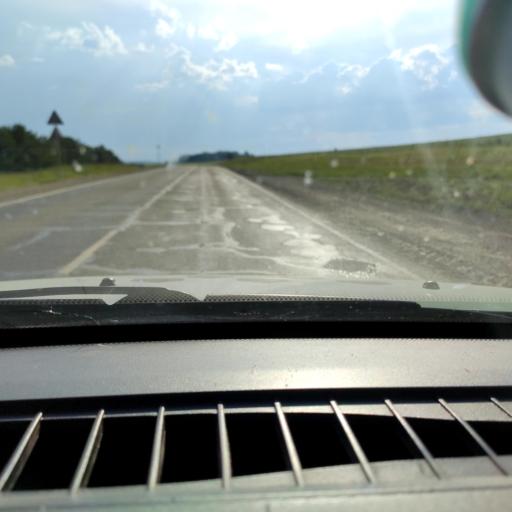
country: RU
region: Udmurtiya
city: Debesy
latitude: 57.6777
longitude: 53.9165
